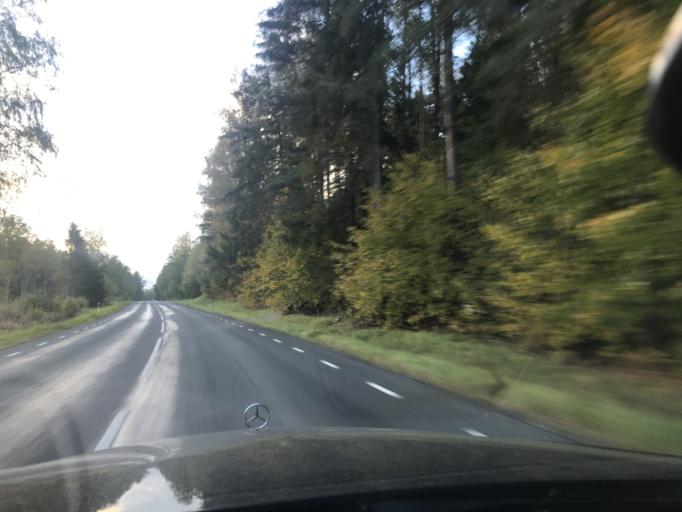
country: EE
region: Vorumaa
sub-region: Antsla vald
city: Vana-Antsla
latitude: 57.8808
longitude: 26.5753
